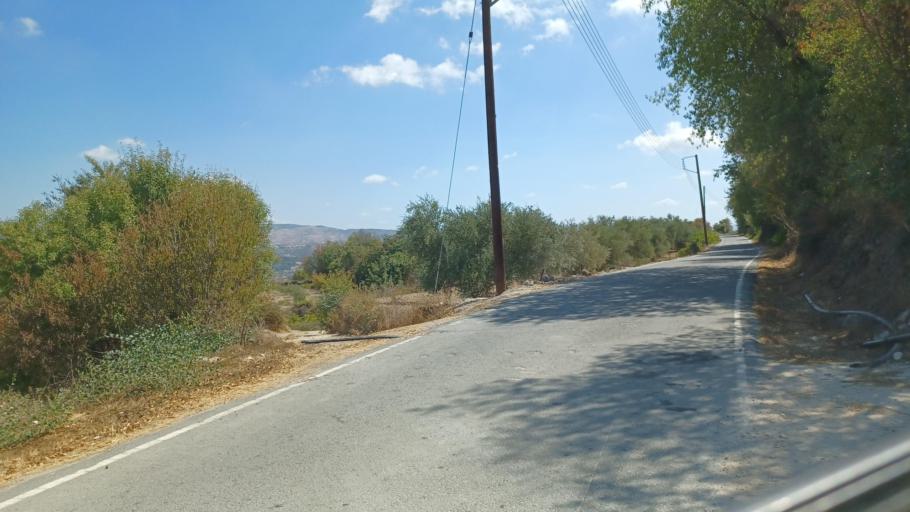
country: CY
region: Pafos
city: Mesogi
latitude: 34.8445
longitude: 32.5294
